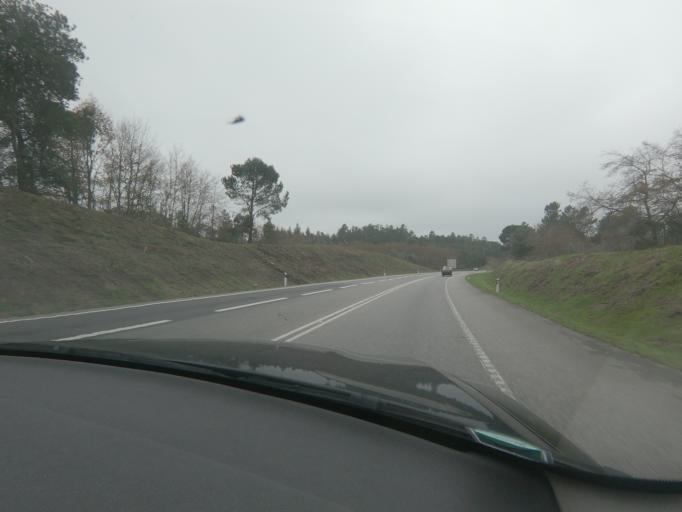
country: PT
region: Viseu
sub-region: Concelho de Tondela
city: Tondela
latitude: 40.5816
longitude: -8.0193
